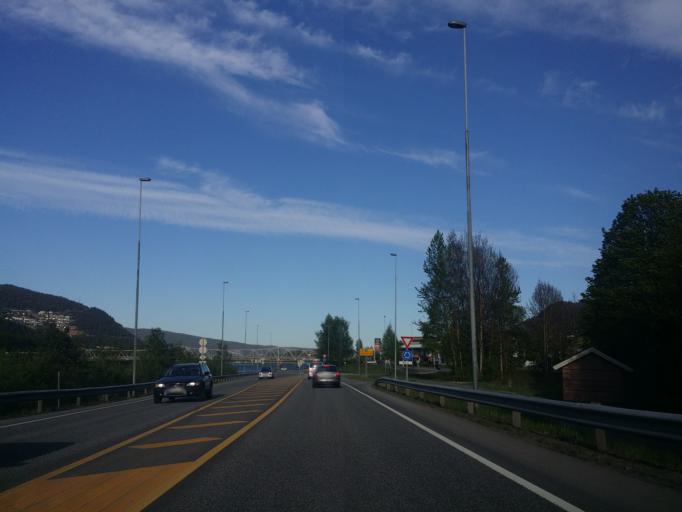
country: NO
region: Buskerud
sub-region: Nedre Eiker
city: Mjondalen
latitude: 59.7527
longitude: 10.0008
